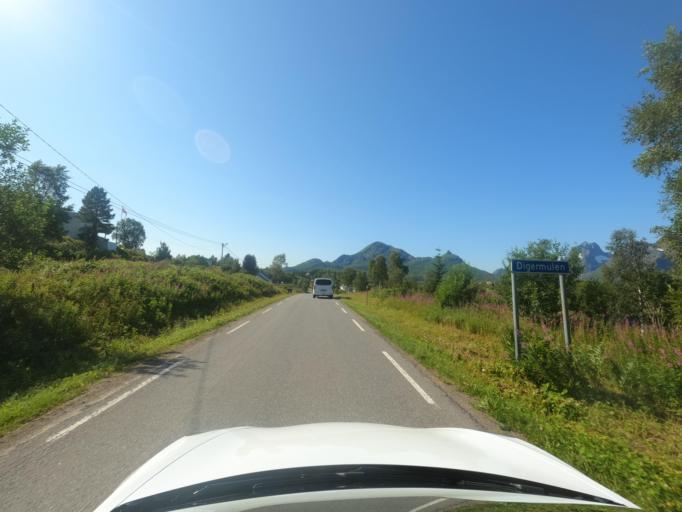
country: NO
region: Nordland
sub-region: Hadsel
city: Stokmarknes
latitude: 68.3162
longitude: 14.9925
